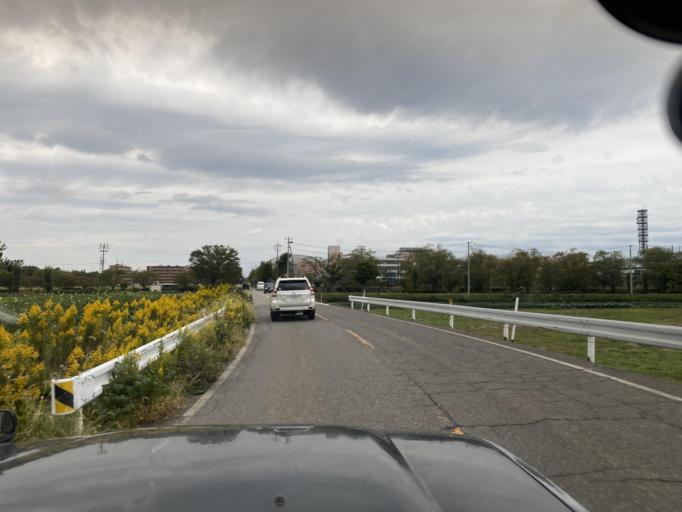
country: JP
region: Niigata
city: Niigata-shi
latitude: 37.8751
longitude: 139.0500
